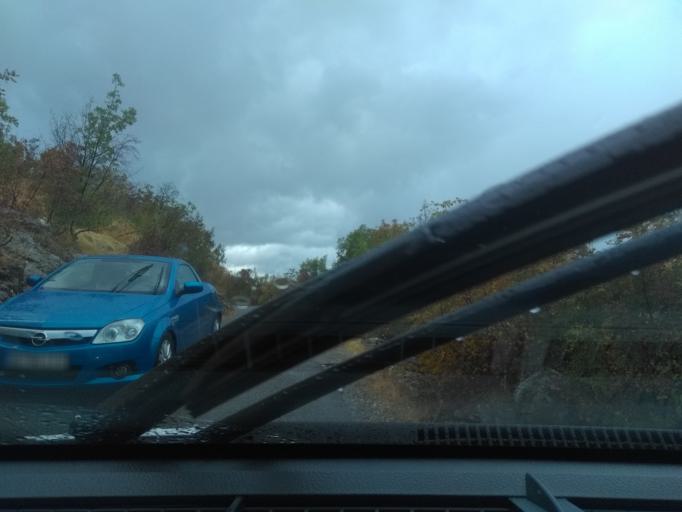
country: ME
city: Stari Bar
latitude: 42.1807
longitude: 19.1798
